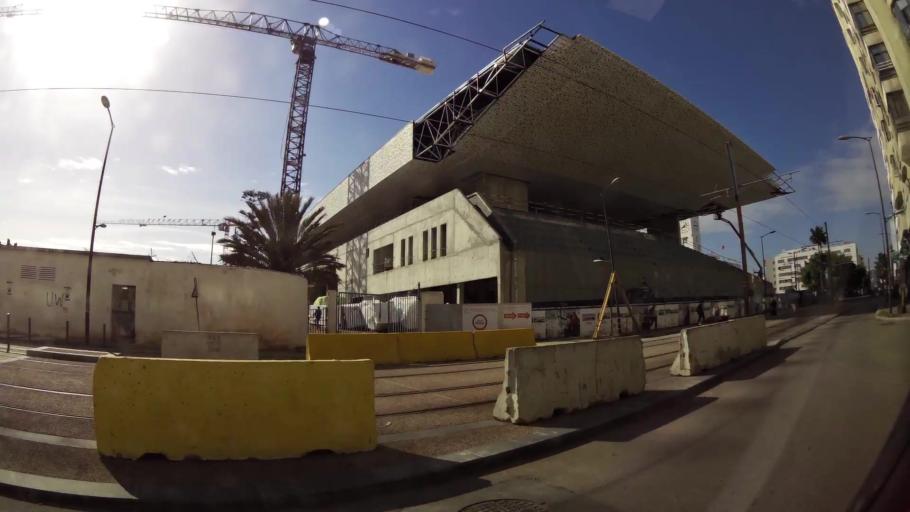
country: MA
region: Grand Casablanca
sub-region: Casablanca
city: Casablanca
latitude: 33.5911
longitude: -7.5905
